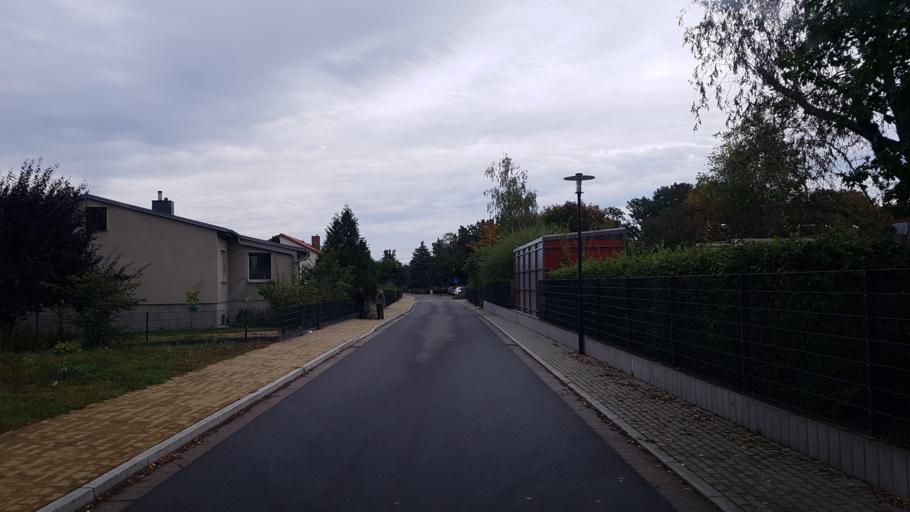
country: DE
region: Brandenburg
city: Baruth
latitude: 52.0427
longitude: 13.5116
